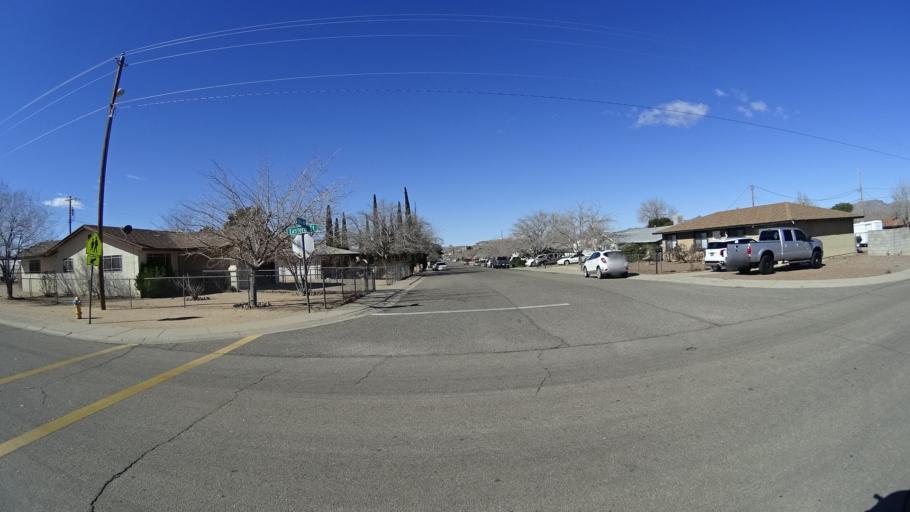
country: US
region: Arizona
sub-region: Mohave County
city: Kingman
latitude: 35.1939
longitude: -114.0114
